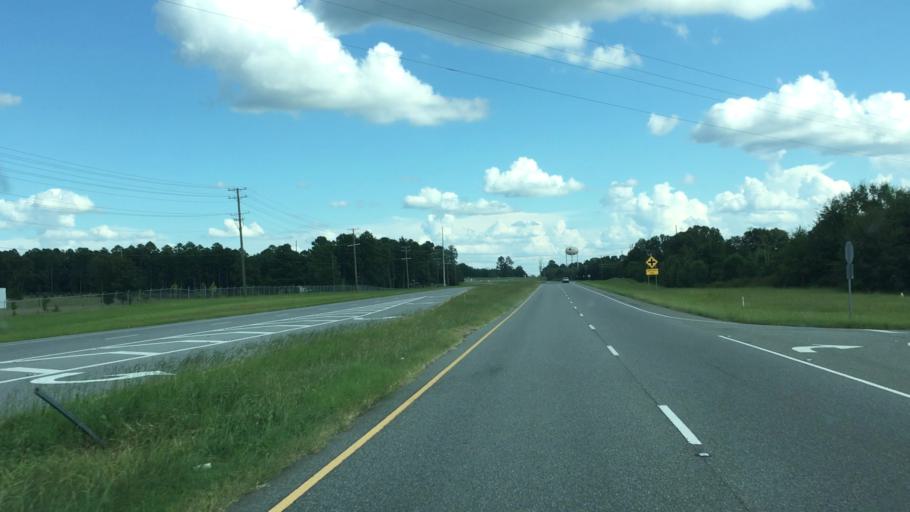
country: US
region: Georgia
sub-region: Laurens County
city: Dublin
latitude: 32.5067
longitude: -82.9462
